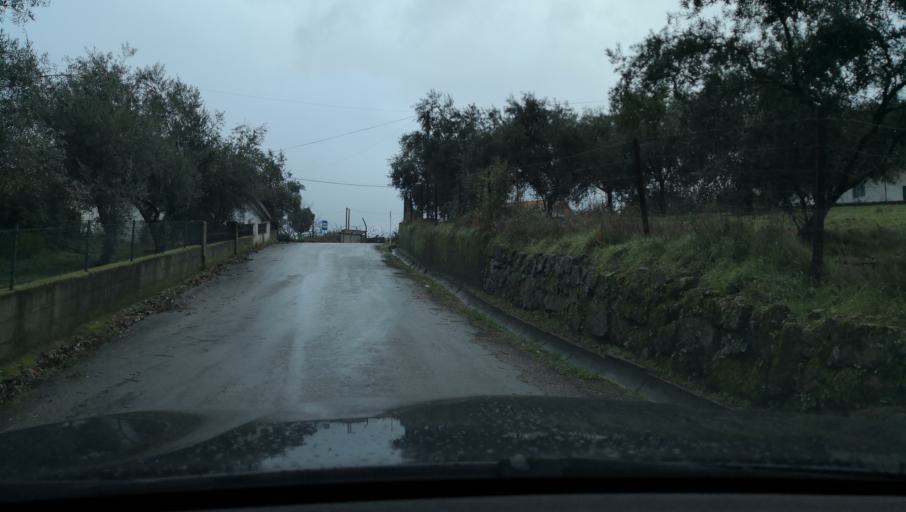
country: PT
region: Vila Real
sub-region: Vila Real
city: Vila Real
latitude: 41.3308
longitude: -7.7251
